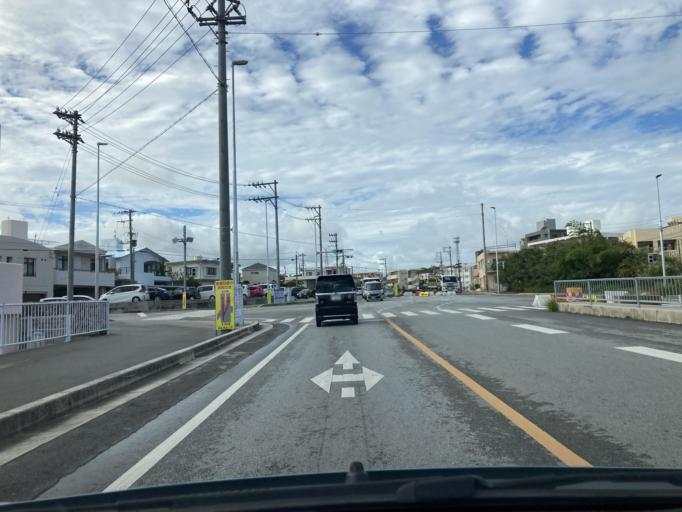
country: JP
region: Okinawa
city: Tomigusuku
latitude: 26.1513
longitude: 127.7226
